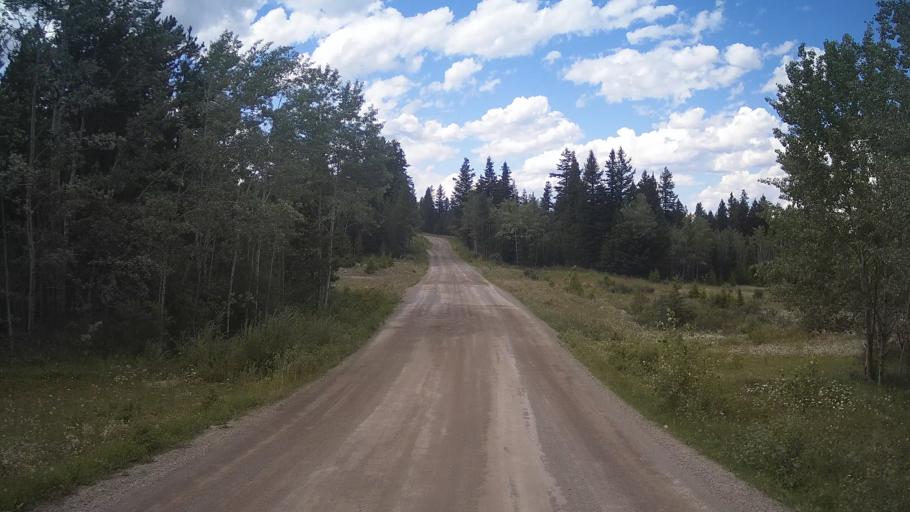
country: CA
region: British Columbia
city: Lillooet
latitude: 51.3109
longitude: -121.8456
